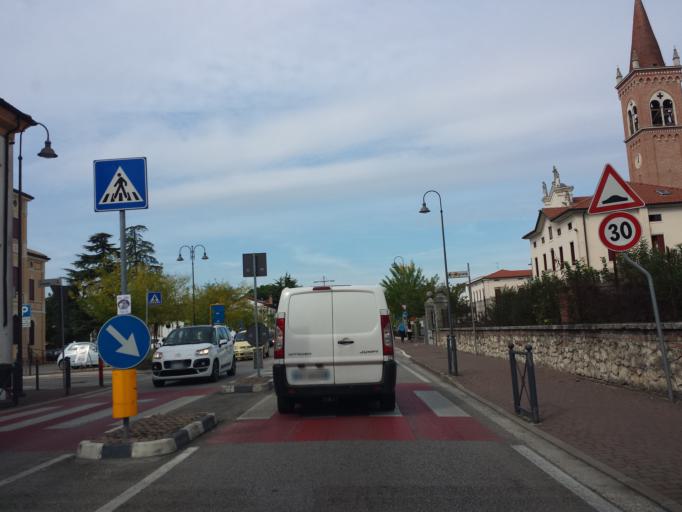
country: IT
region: Veneto
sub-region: Provincia di Vicenza
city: Torri di Quartesolo
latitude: 45.5196
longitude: 11.6170
